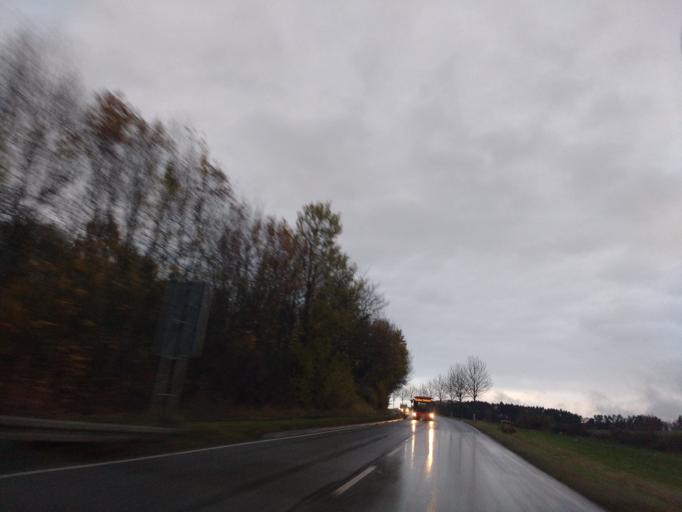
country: DE
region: Hesse
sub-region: Regierungsbezirk Kassel
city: Martinhagen
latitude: 51.2823
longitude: 9.3248
